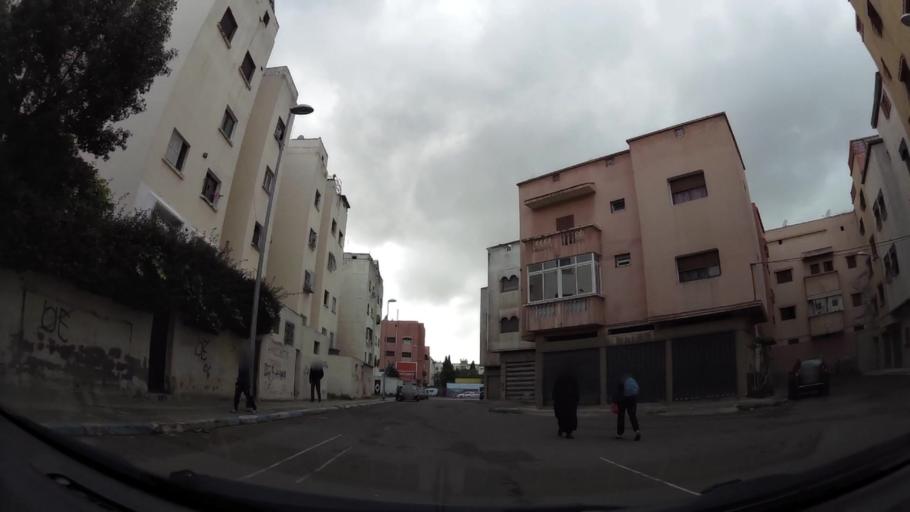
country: MA
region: Grand Casablanca
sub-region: Casablanca
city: Casablanca
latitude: 33.5430
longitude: -7.5875
